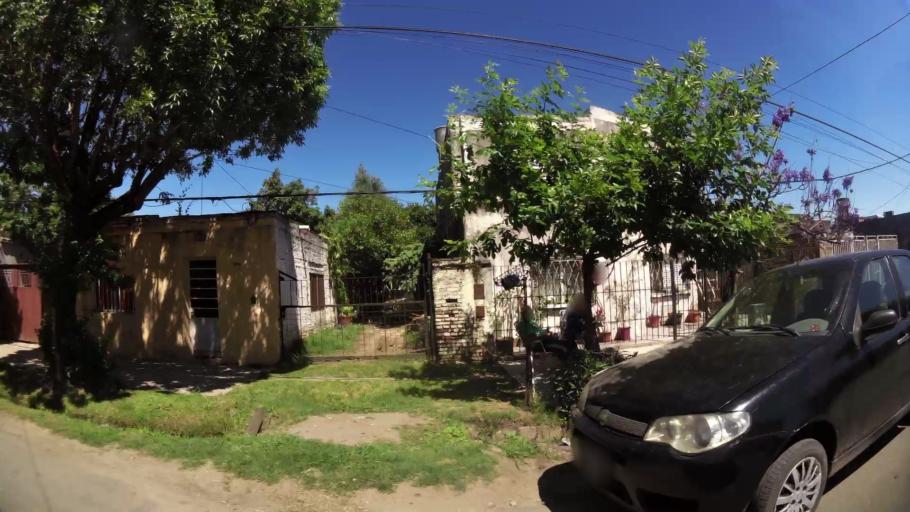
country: AR
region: Santa Fe
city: Perez
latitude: -32.9545
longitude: -60.7201
